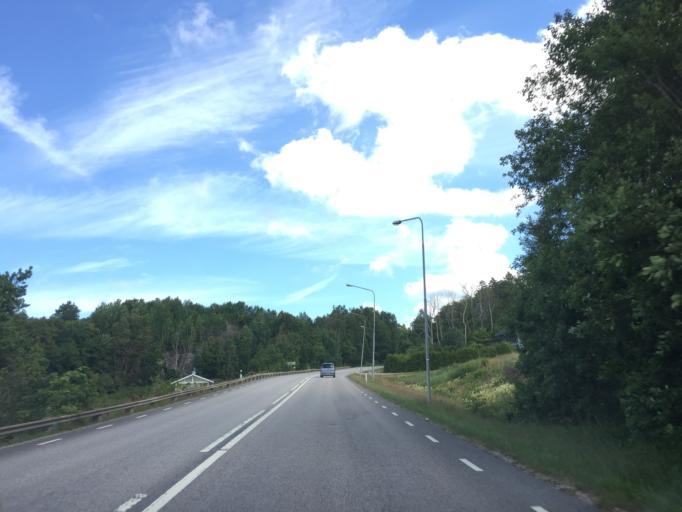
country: SE
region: Vaestra Goetaland
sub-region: Orust
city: Henan
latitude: 58.2418
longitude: 11.6810
